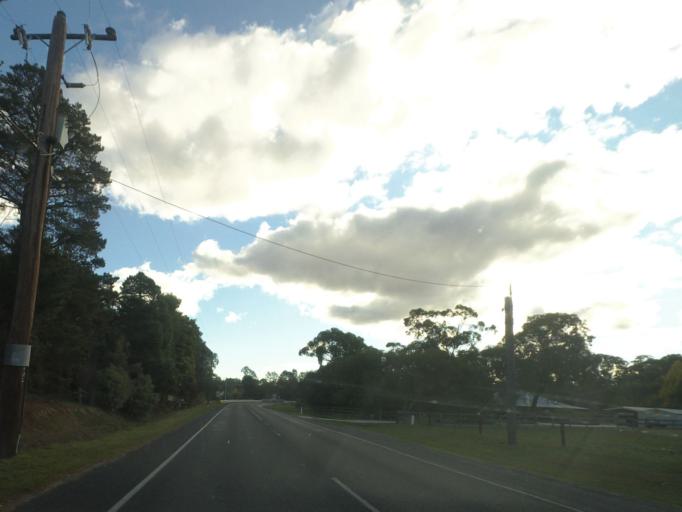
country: AU
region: Victoria
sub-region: Mount Alexander
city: Castlemaine
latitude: -37.0846
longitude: 144.2712
